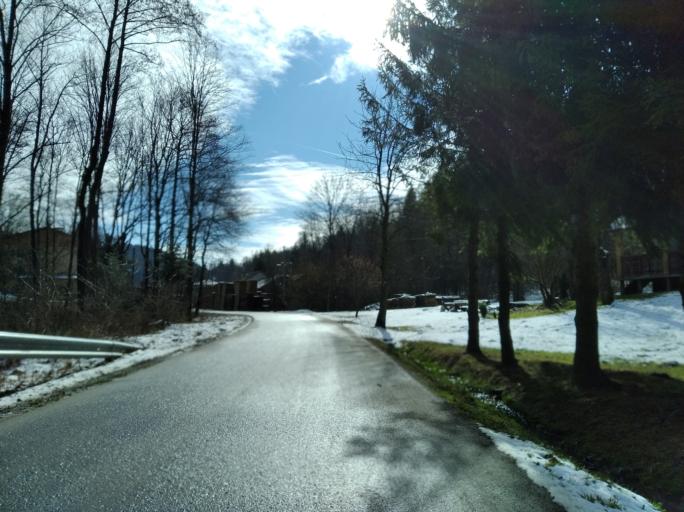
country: PL
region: Subcarpathian Voivodeship
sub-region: Powiat brzozowski
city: Jablonica Polska
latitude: 49.7473
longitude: 21.8805
